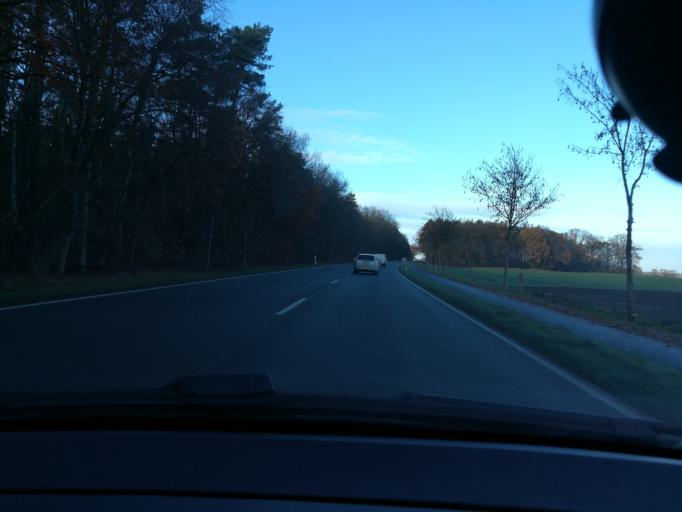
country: DE
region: Lower Saxony
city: Kirchdorf
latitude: 52.5832
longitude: 8.8388
